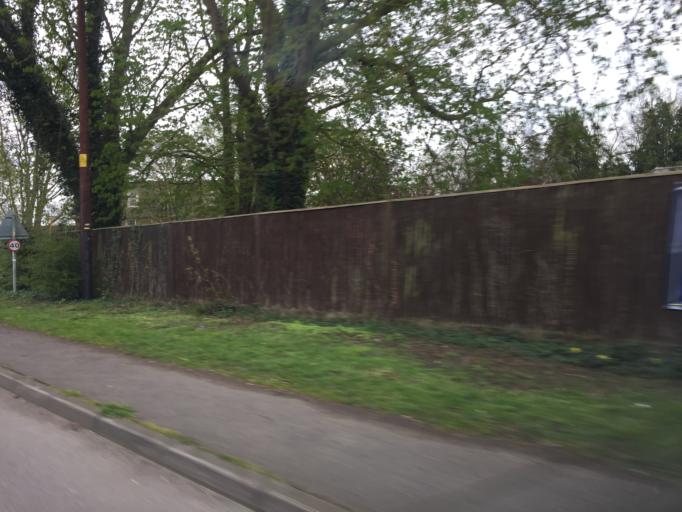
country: GB
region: England
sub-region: Oxfordshire
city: Bicester
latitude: 51.9195
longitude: -1.1505
